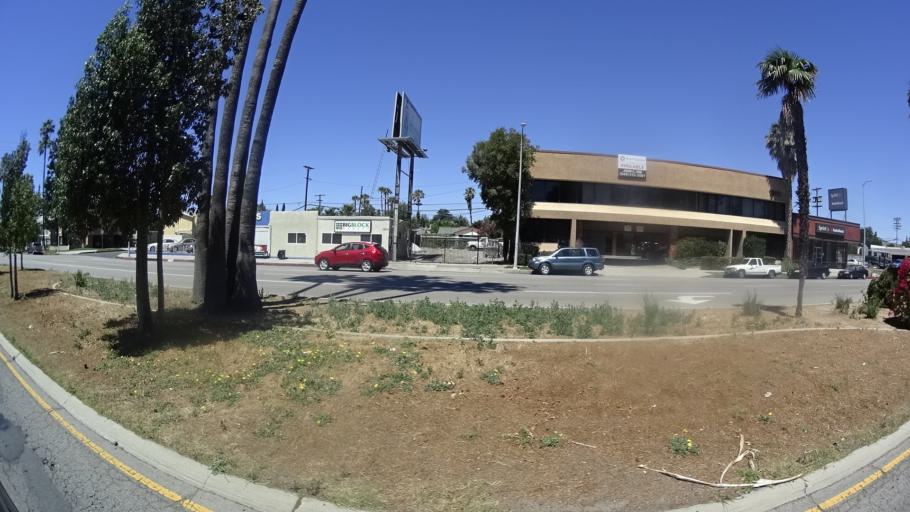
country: US
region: California
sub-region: Los Angeles County
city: San Fernando
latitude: 34.2540
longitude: -118.4675
